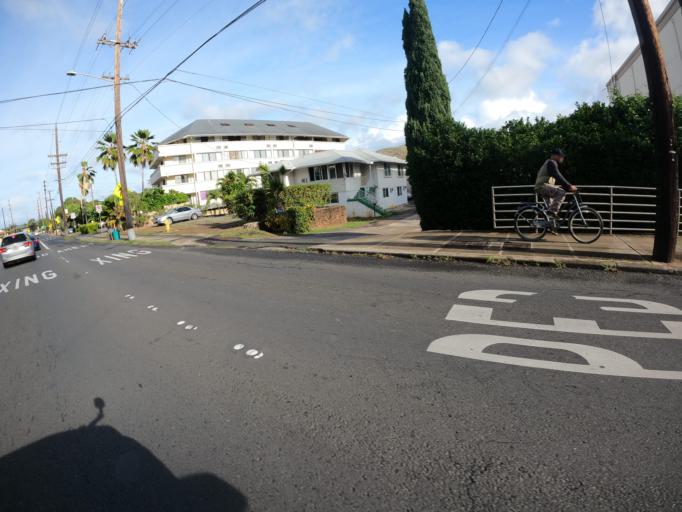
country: US
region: Hawaii
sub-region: Honolulu County
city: Honolulu
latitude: 21.2898
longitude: -157.8141
